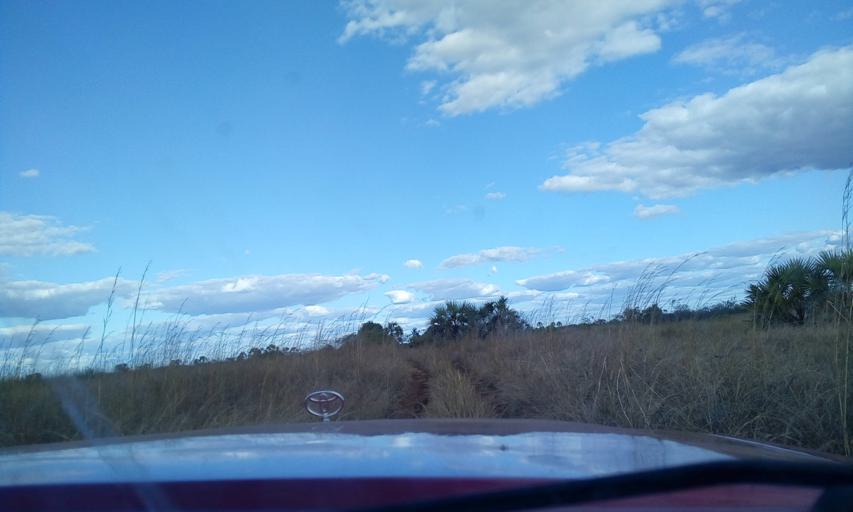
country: MG
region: Melaky
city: Mahabe
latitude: -16.4119
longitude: 45.3658
